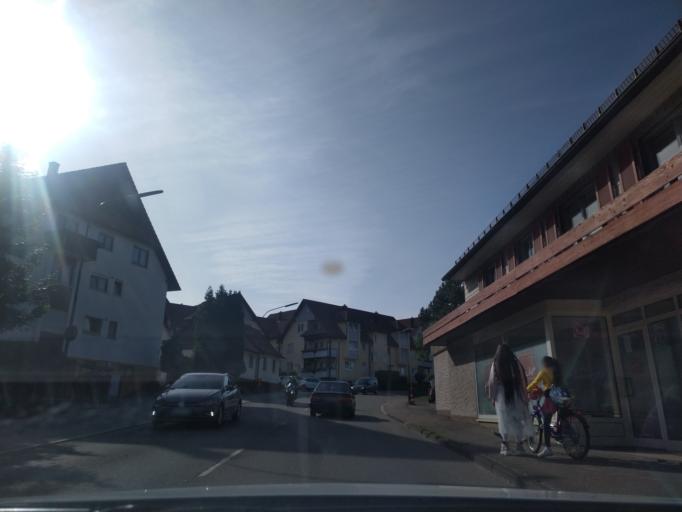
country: DE
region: Baden-Wuerttemberg
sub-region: Karlsruhe Region
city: Lossburg
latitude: 48.4173
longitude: 8.4455
